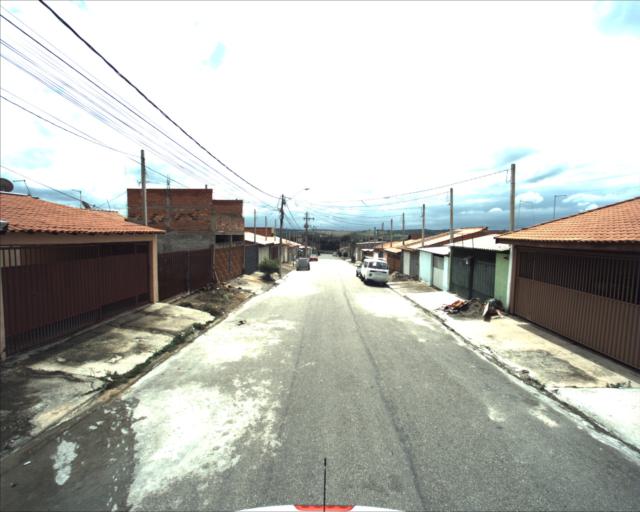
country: BR
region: Sao Paulo
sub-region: Sorocaba
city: Sorocaba
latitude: -23.4232
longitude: -47.4644
